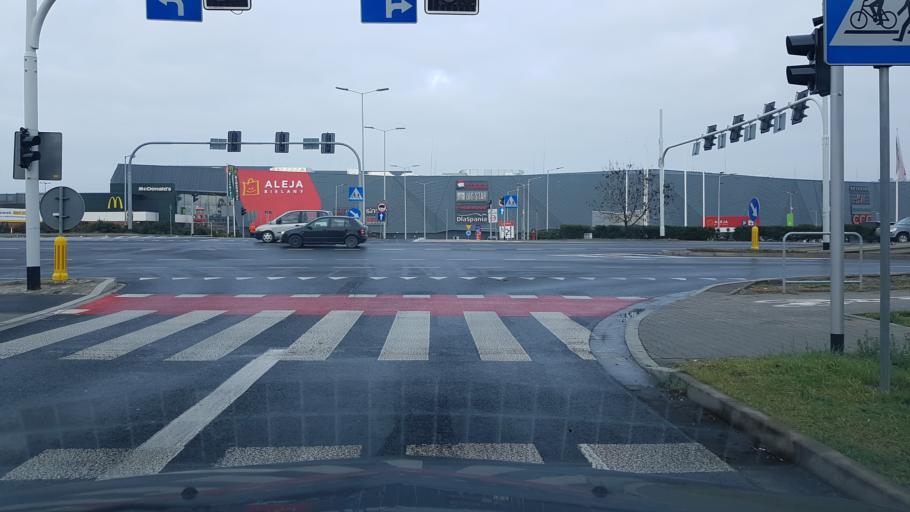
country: PL
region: Lower Silesian Voivodeship
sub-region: Powiat wroclawski
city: Bielany Wroclawskie
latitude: 51.0468
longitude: 16.9592
